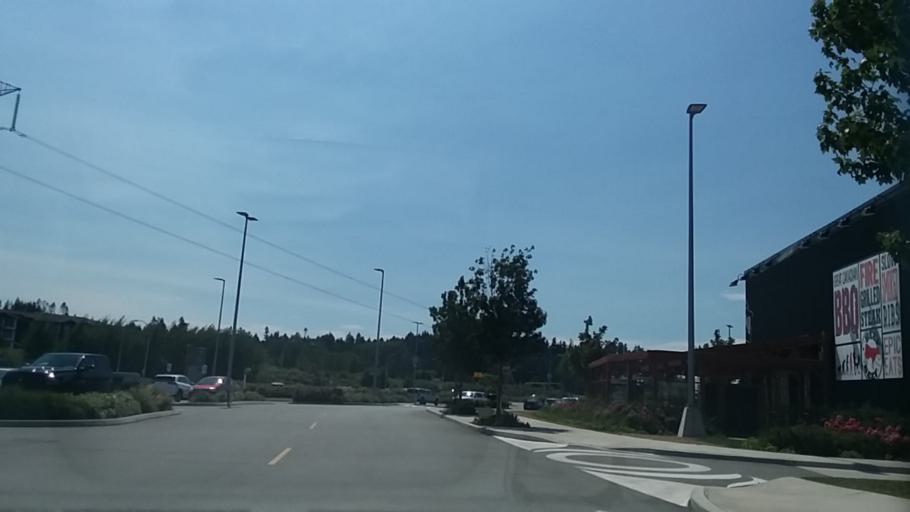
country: US
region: Washington
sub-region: Whatcom County
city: Point Roberts
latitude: 49.0352
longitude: -123.0872
